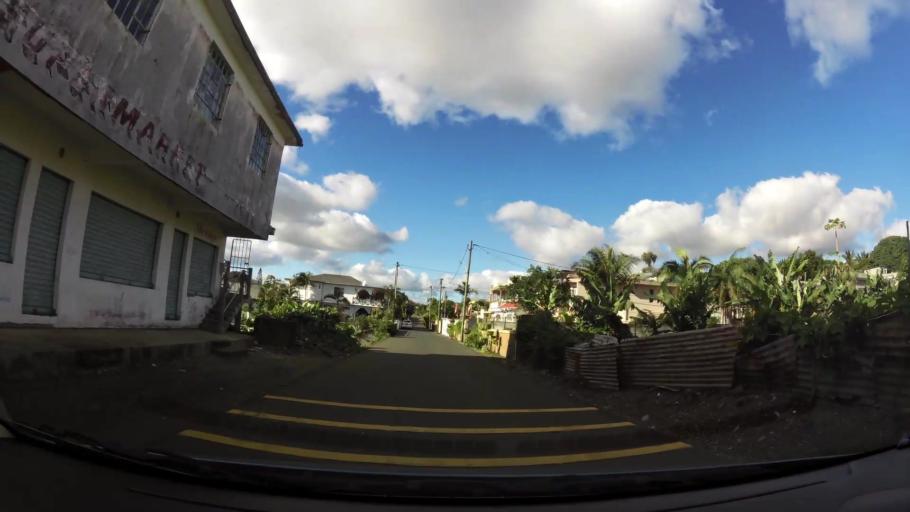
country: MU
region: Plaines Wilhems
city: Vacoas
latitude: -20.2884
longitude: 57.4941
